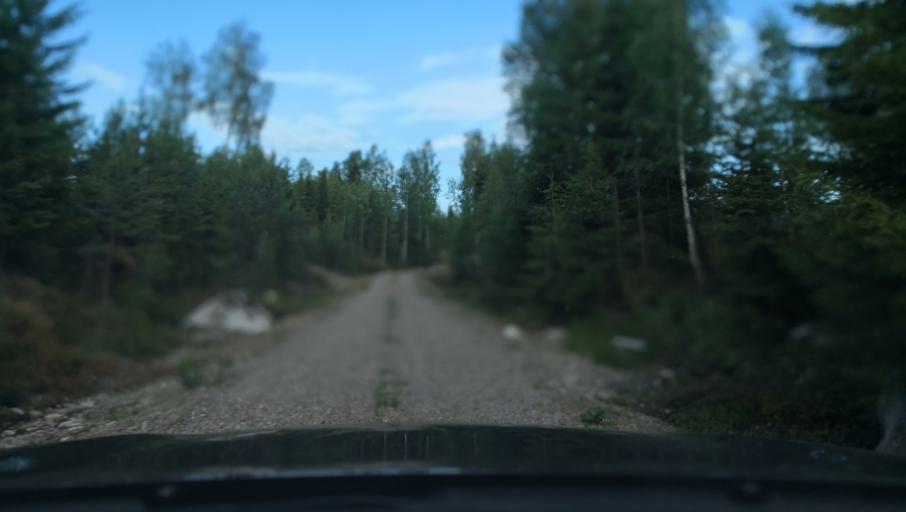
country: SE
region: Dalarna
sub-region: Smedjebackens Kommun
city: Smedjebacken
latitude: 60.0698
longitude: 15.3002
